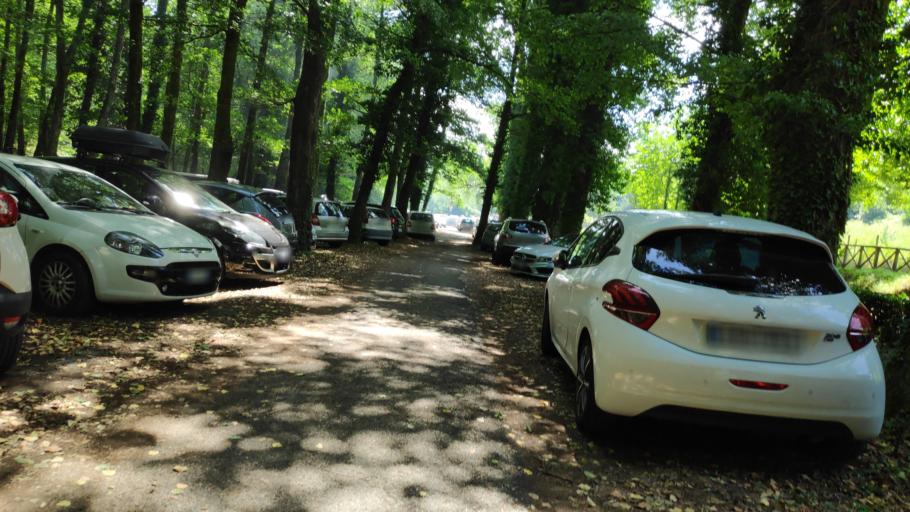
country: IT
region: Calabria
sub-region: Provincia di Vibo-Valentia
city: Serra San Bruno
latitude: 38.5577
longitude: 16.3141
